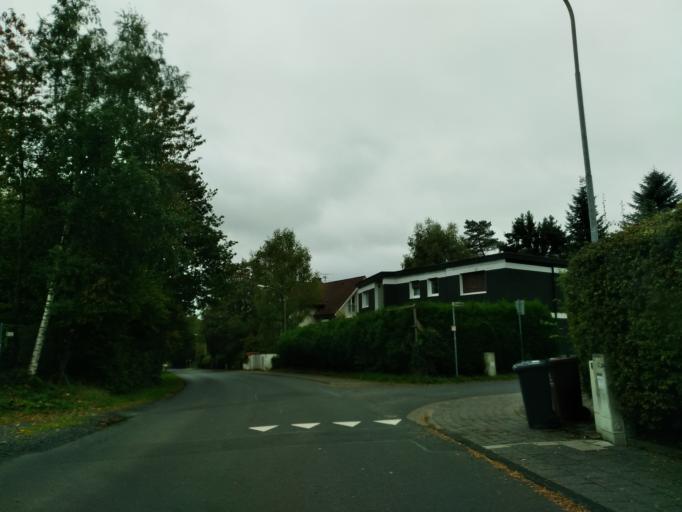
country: DE
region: Rheinland-Pfalz
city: Windhagen
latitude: 50.6442
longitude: 7.3127
